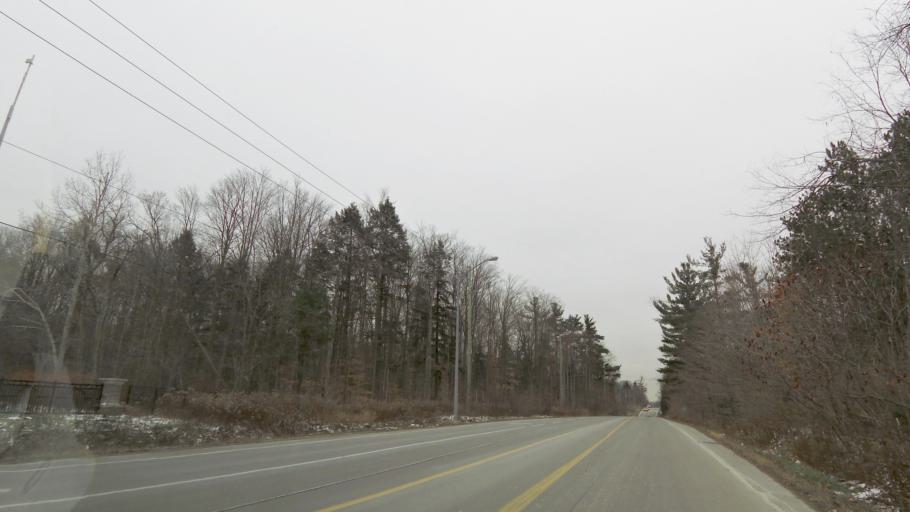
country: CA
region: Ontario
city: Vaughan
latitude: 43.8326
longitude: -79.5848
